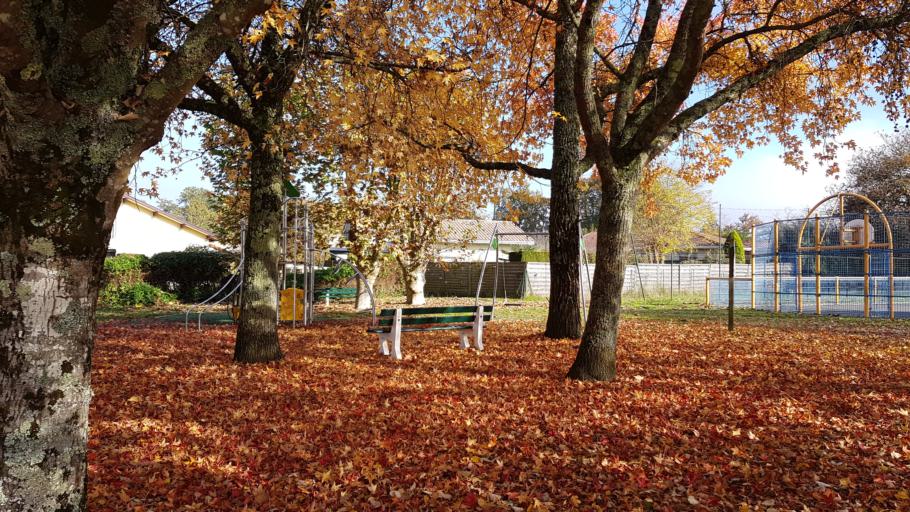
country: FR
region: Aquitaine
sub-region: Departement des Landes
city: Saint-Paul-les-Dax
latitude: 43.7338
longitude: -1.0605
